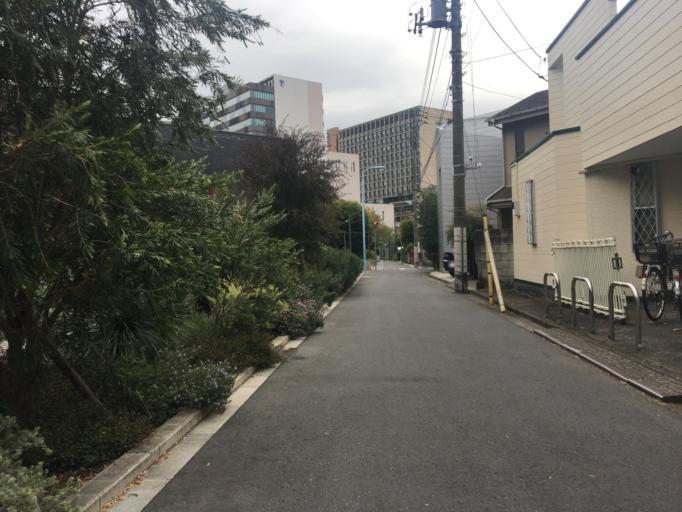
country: JP
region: Tokyo
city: Tokyo
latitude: 35.7084
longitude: 139.6570
